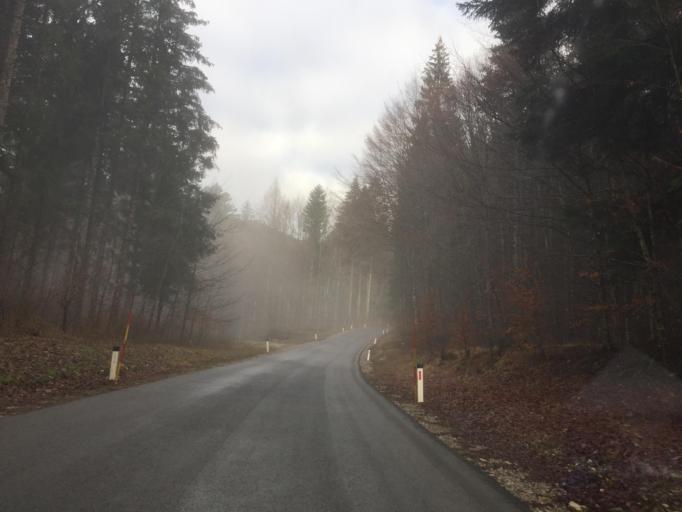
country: SI
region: Ajdovscina
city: Lokavec
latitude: 45.9583
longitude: 13.8553
